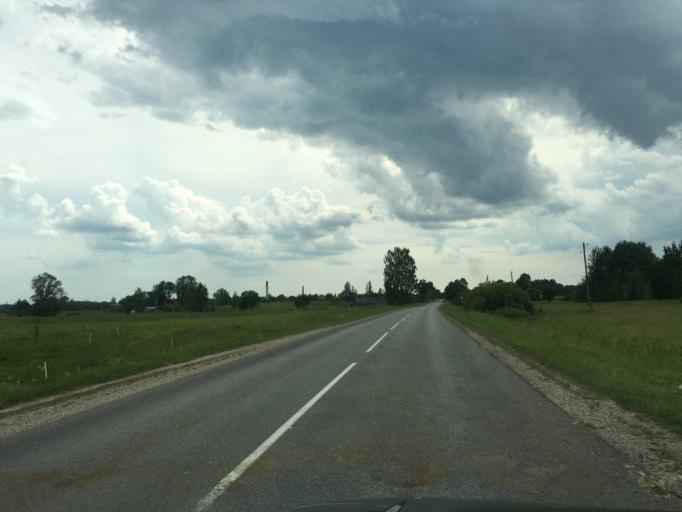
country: LV
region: Rugaju
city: Rugaji
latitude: 56.9172
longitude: 27.0706
